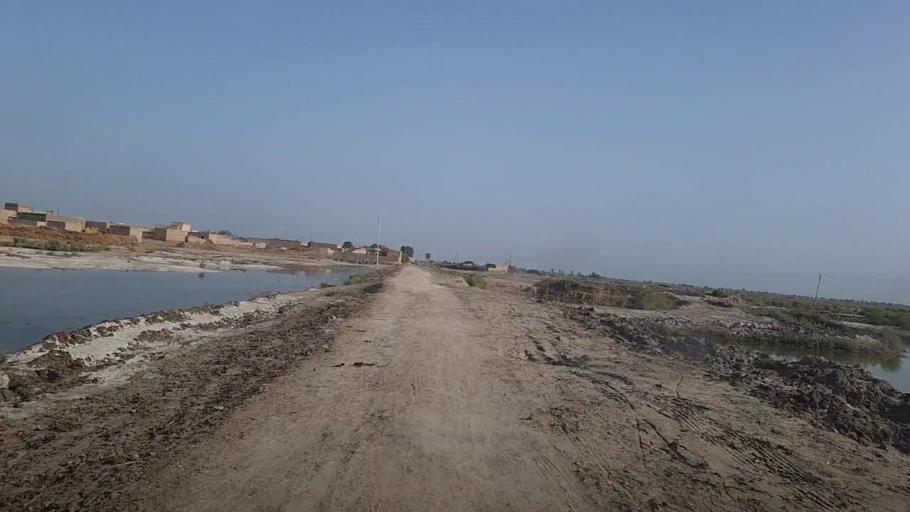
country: PK
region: Sindh
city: Sita Road
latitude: 27.1120
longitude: 67.8825
